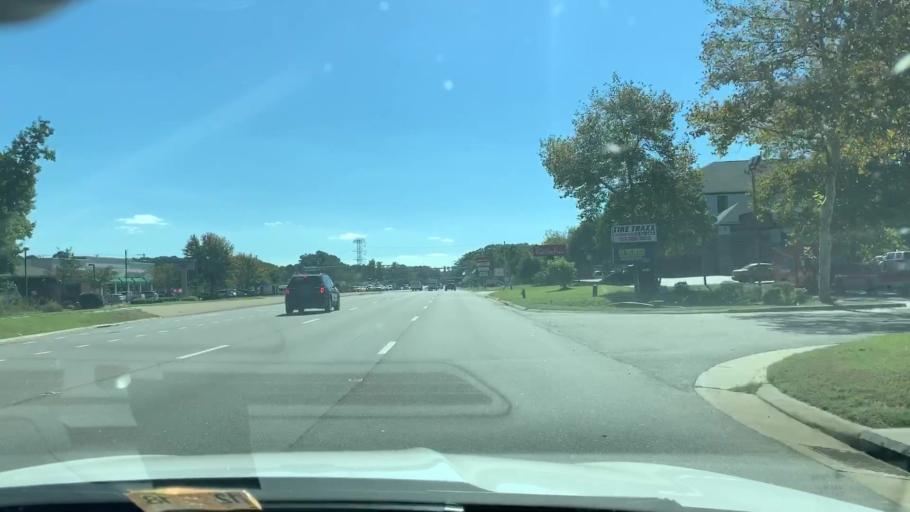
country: US
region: Virginia
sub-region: York County
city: Yorktown
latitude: 37.1493
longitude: -76.4598
